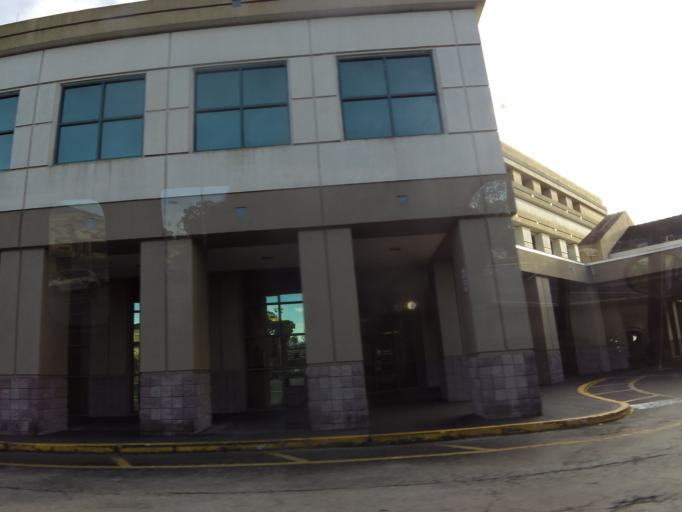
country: US
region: Florida
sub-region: Saint Johns County
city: Fruit Cove
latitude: 30.1591
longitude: -81.6315
